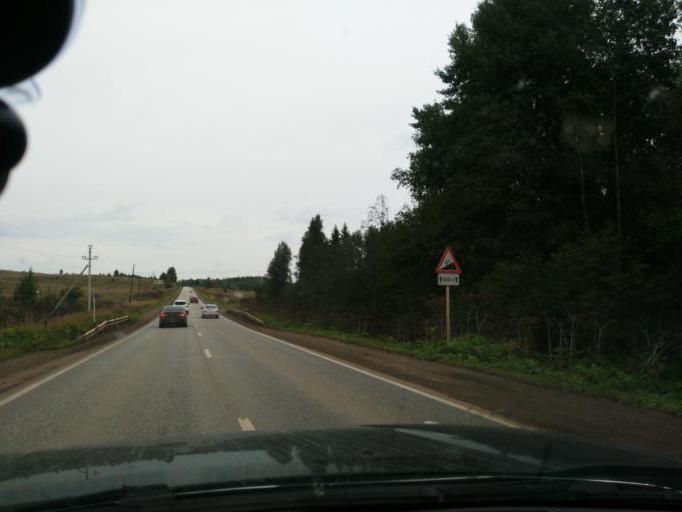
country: RU
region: Perm
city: Chernushka
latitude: 56.5721
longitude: 56.1279
